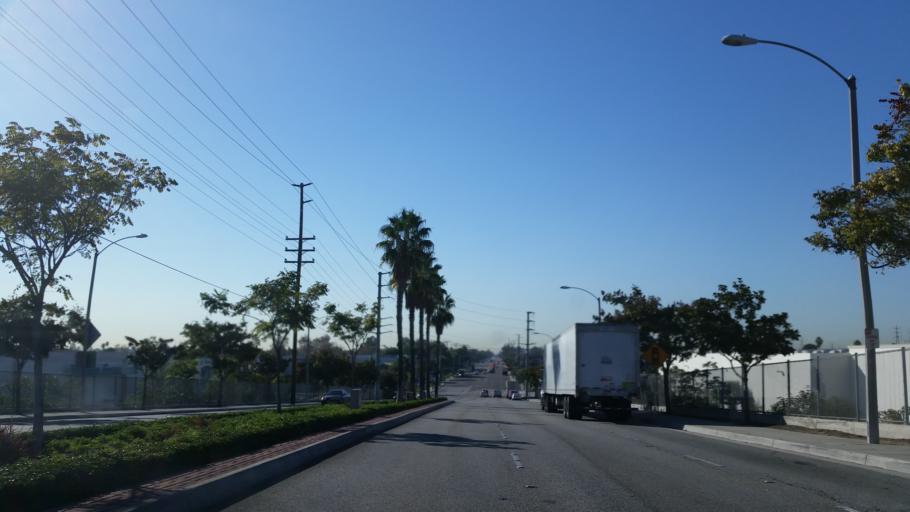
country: US
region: California
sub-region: Orange County
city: Buena Park
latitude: 33.8533
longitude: -117.9763
